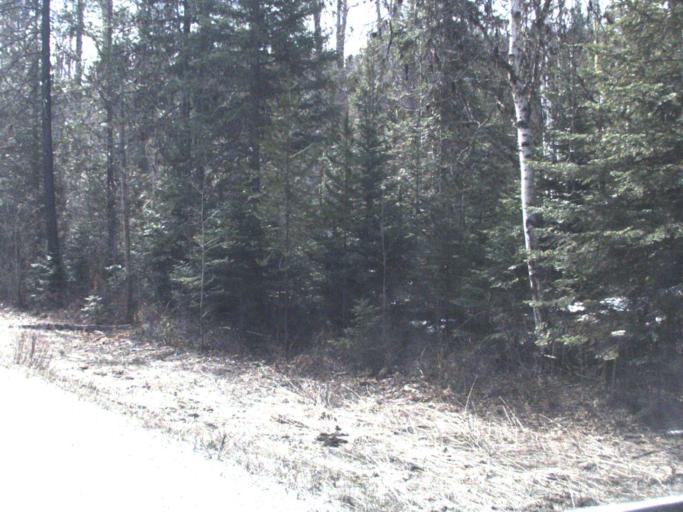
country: US
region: Washington
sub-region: Stevens County
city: Chewelah
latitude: 48.5936
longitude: -117.3549
